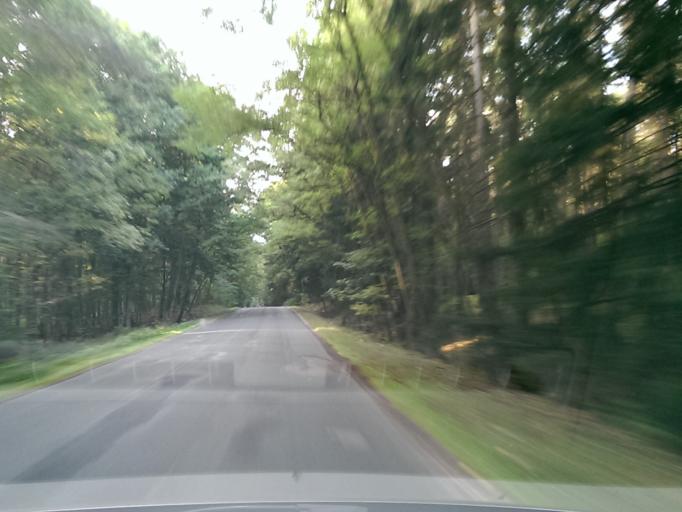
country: CZ
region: Central Bohemia
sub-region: Okres Mlada Boleslav
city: Zd'ar
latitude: 50.5199
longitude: 15.1088
